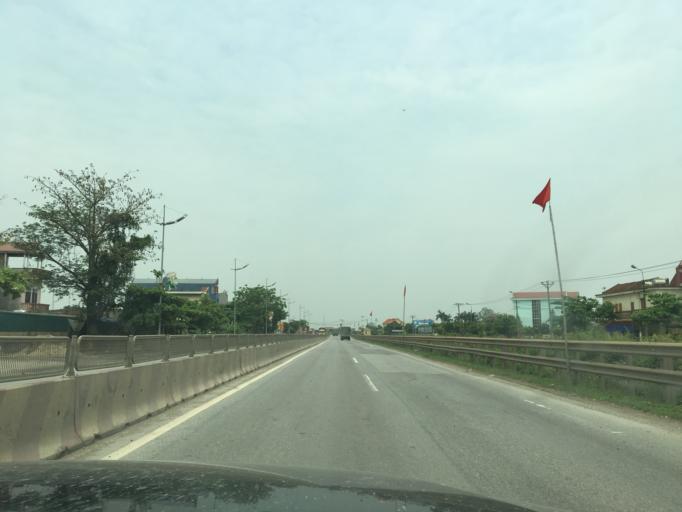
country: VN
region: Ninh Binh
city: Thi Tran Tam Diep
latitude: 20.1640
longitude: 105.9344
